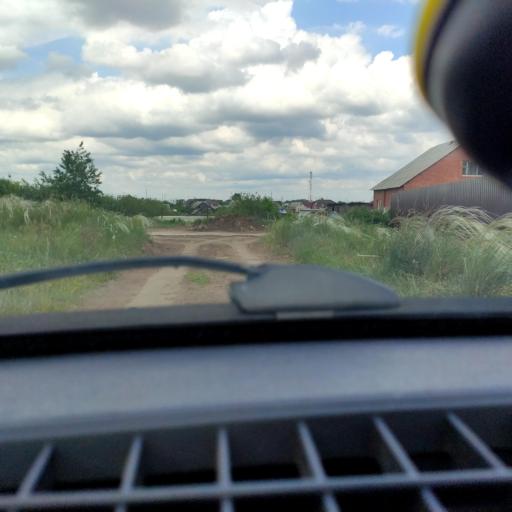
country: RU
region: Samara
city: Povolzhskiy
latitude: 53.6321
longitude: 49.6664
